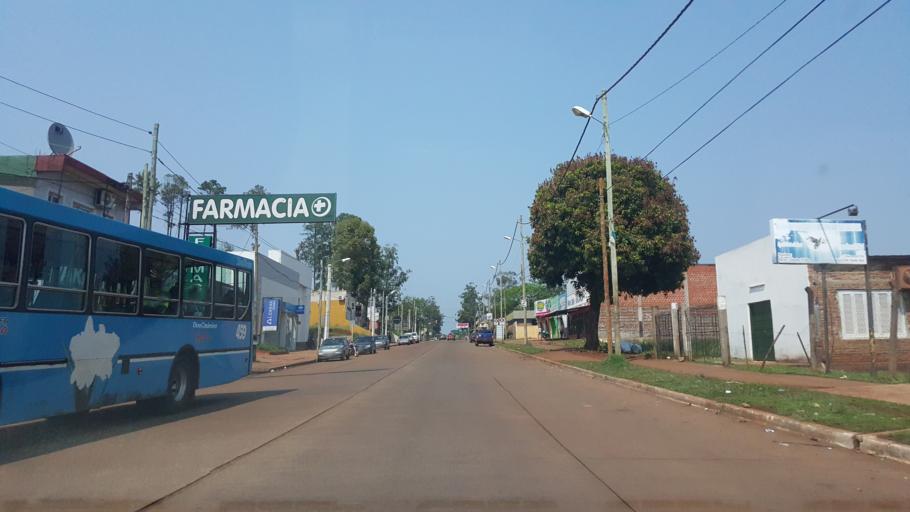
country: AR
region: Misiones
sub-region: Departamento de Capital
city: Posadas
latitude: -27.4129
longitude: -55.9556
